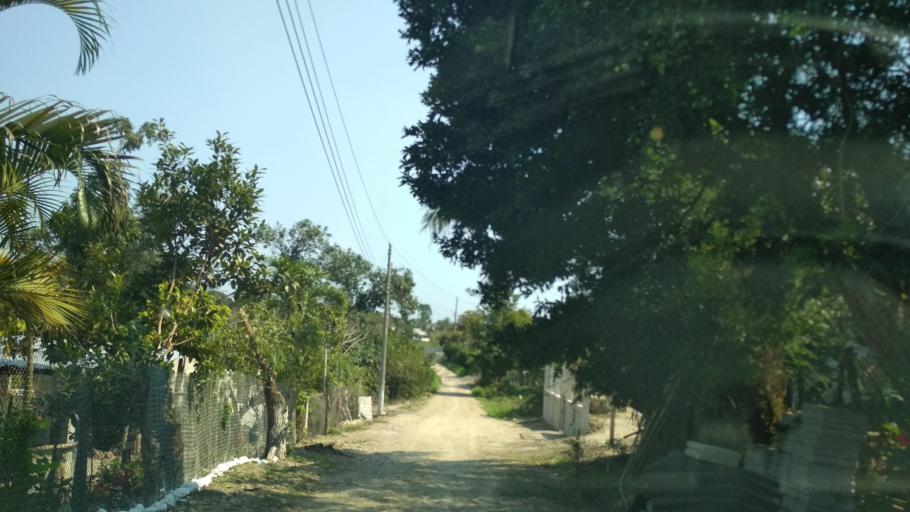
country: MX
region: Veracruz
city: Gutierrez Zamora
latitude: 20.4242
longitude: -97.1945
